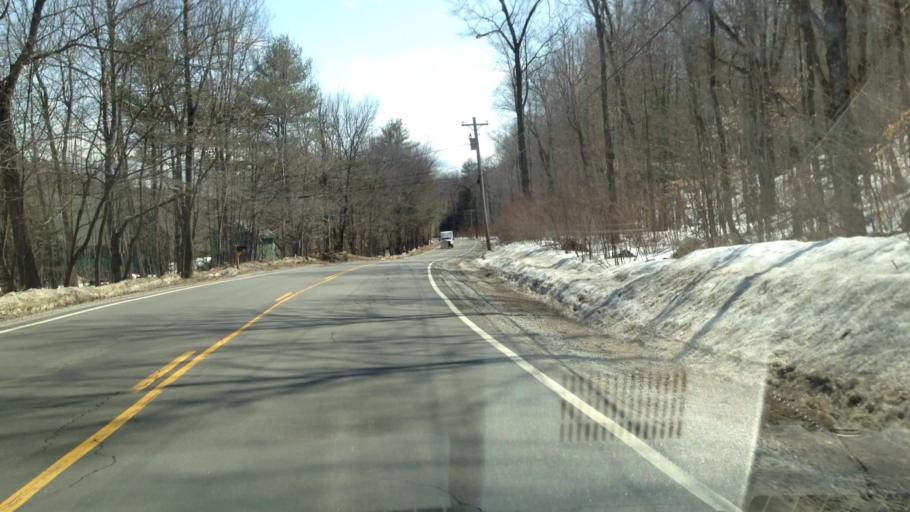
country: US
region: New Hampshire
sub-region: Merrimack County
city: Wilmot
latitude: 43.4617
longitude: -71.9438
